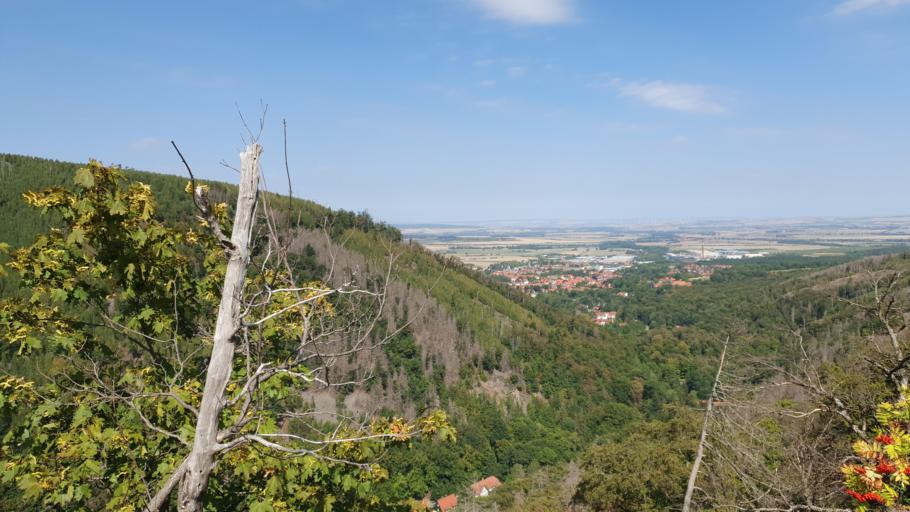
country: DE
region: Saxony-Anhalt
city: Ilsenburg
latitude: 51.8466
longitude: 10.6623
